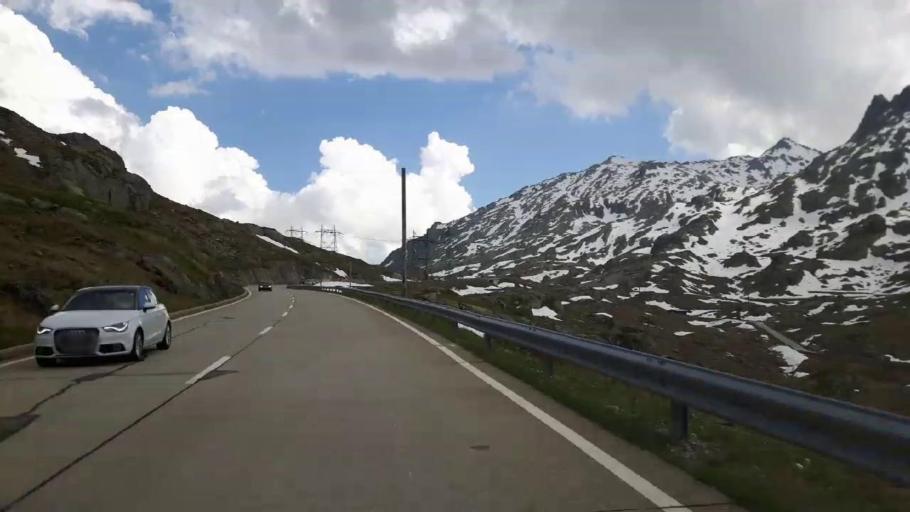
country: CH
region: Ticino
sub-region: Leventina District
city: Airolo
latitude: 46.5674
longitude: 8.5605
